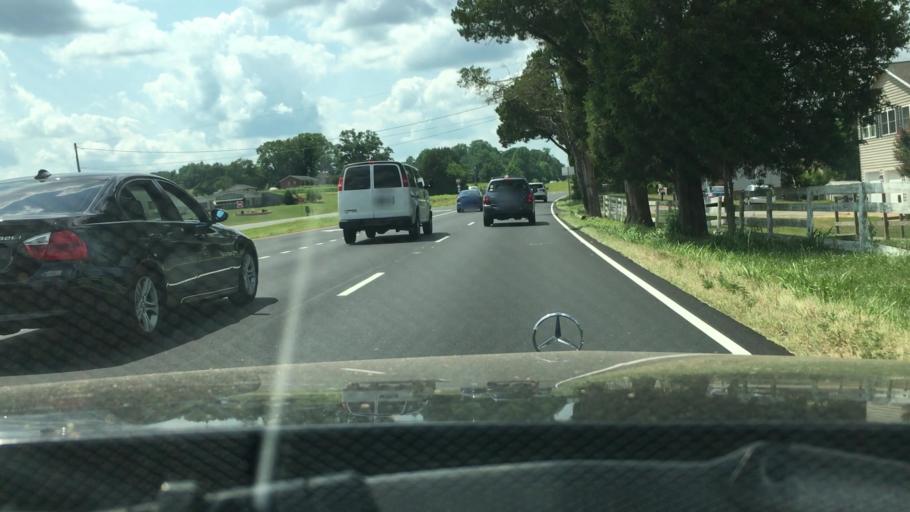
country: US
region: Virginia
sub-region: Spotsylvania County
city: Spotsylvania
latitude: 38.2976
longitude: -77.6060
